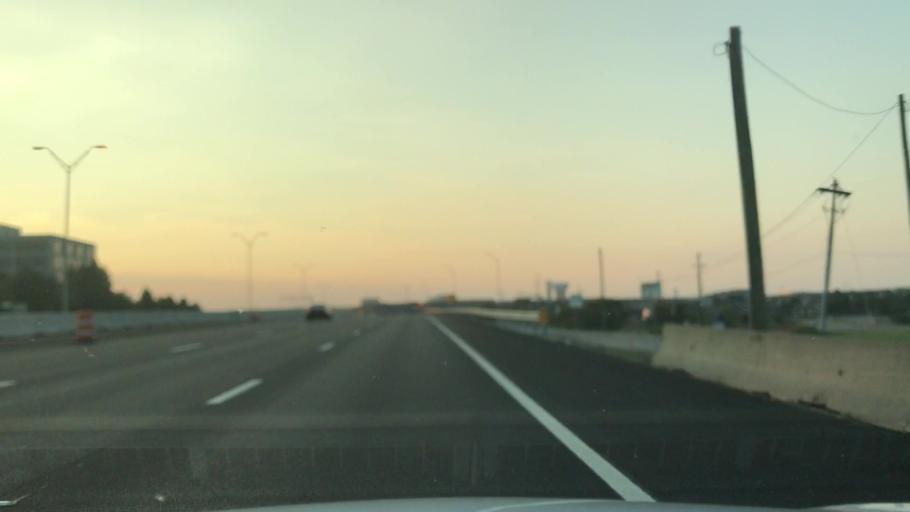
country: US
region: Texas
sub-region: Dallas County
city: Coppell
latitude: 32.8995
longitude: -96.9789
